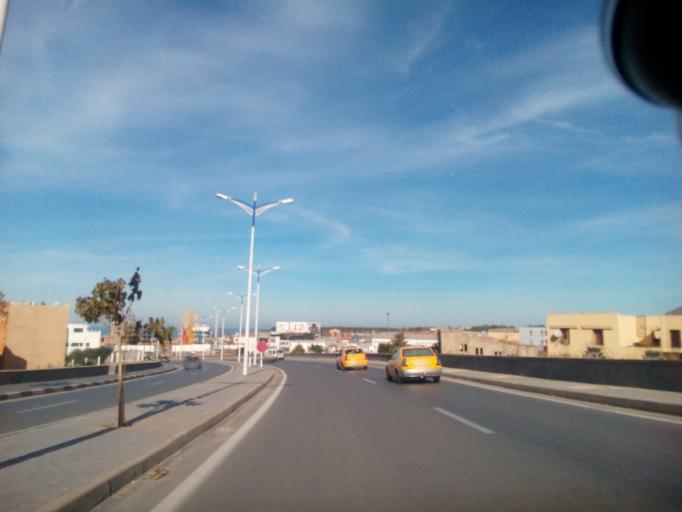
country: DZ
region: Mostaganem
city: Mostaganem
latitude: 35.9517
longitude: 0.0960
